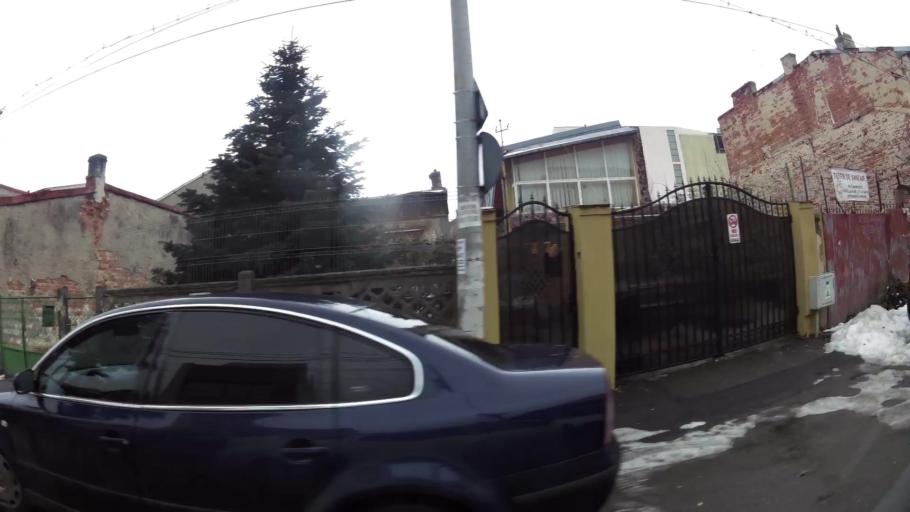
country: RO
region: Bucuresti
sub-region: Municipiul Bucuresti
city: Bucuresti
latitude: 44.4539
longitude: 26.0694
